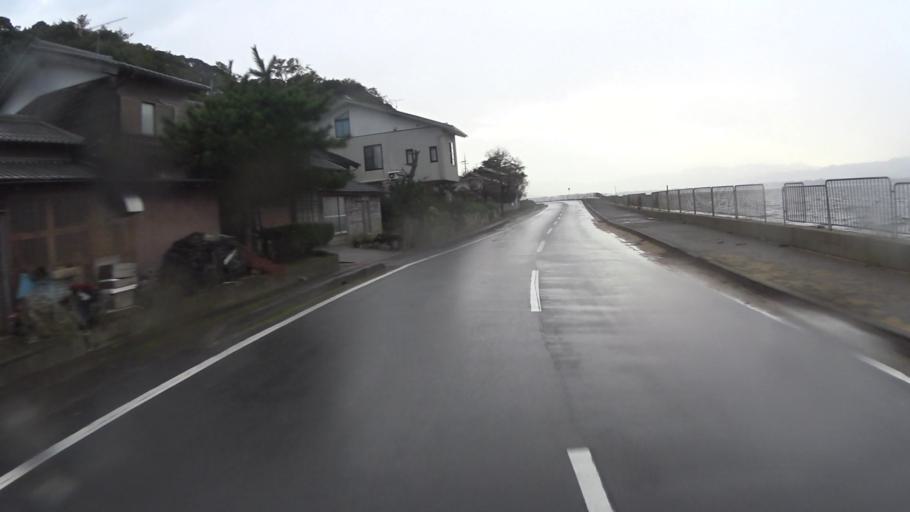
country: JP
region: Kyoto
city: Miyazu
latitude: 35.5662
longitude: 135.2175
